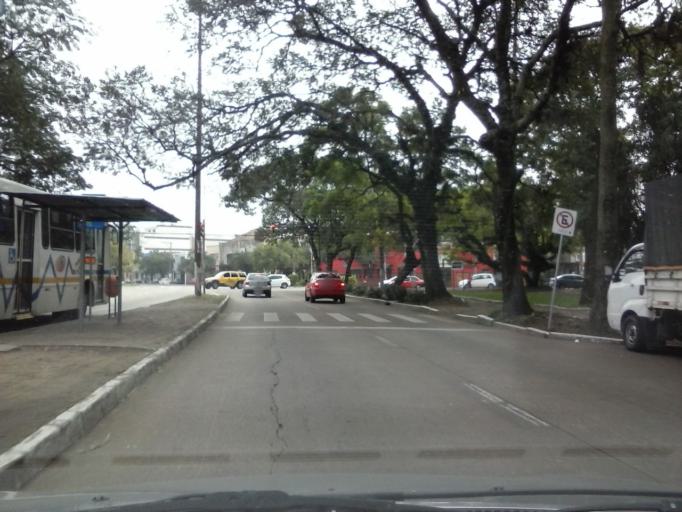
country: BR
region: Rio Grande do Sul
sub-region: Porto Alegre
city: Porto Alegre
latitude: -30.0442
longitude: -51.2203
